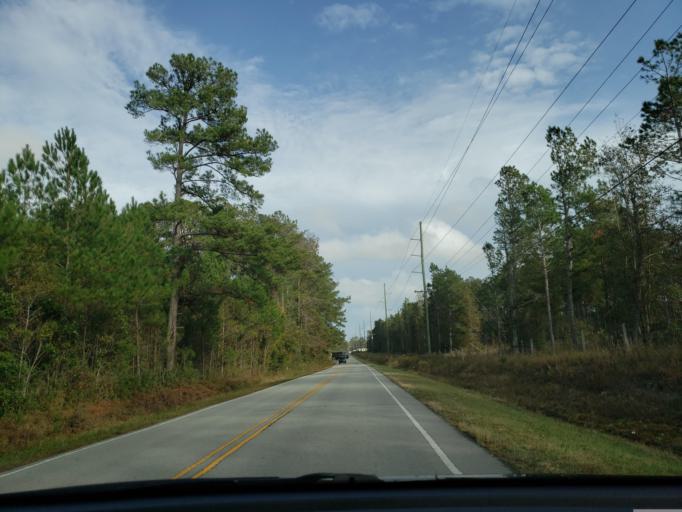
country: US
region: North Carolina
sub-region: Onslow County
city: Jacksonville
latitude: 34.6859
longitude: -77.5180
